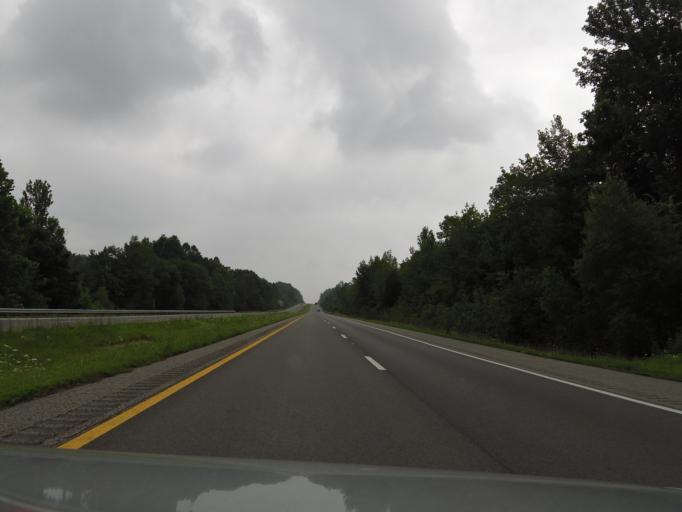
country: US
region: Kentucky
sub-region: Muhlenberg County
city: Morehead
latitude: 37.2483
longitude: -87.2334
